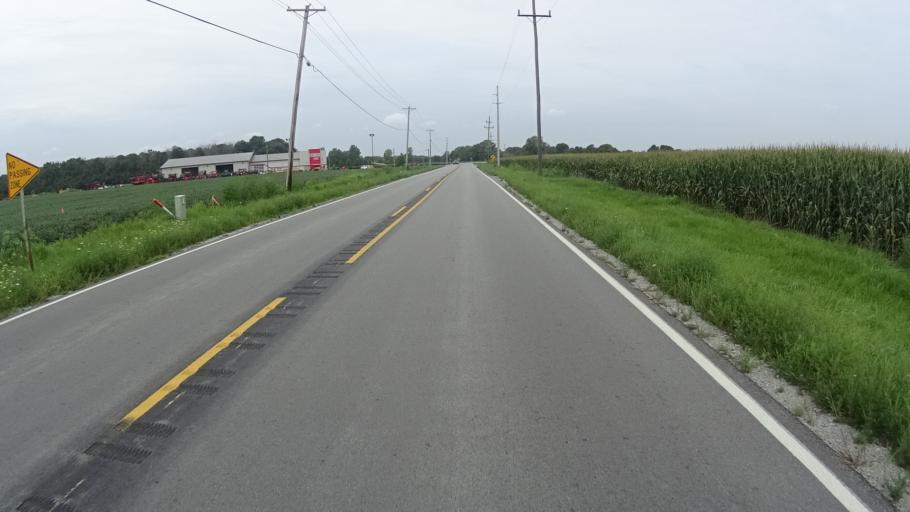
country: US
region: Indiana
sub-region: Madison County
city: Pendleton
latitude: 40.0057
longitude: -85.7792
